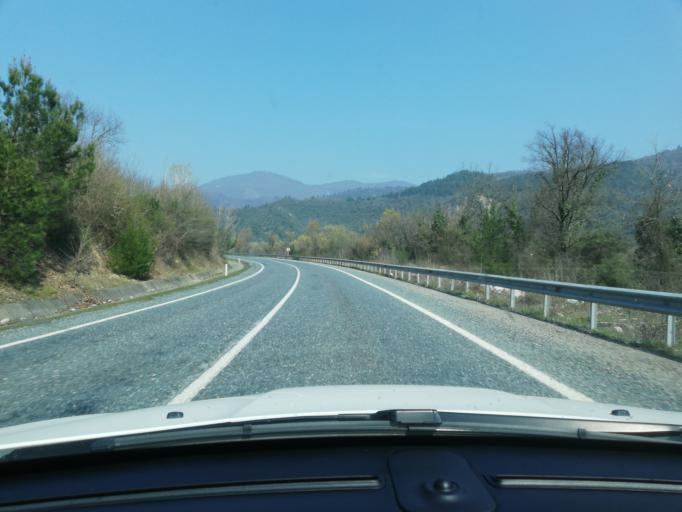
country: TR
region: Zonguldak
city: Gokcebey
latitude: 41.2288
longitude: 32.2121
